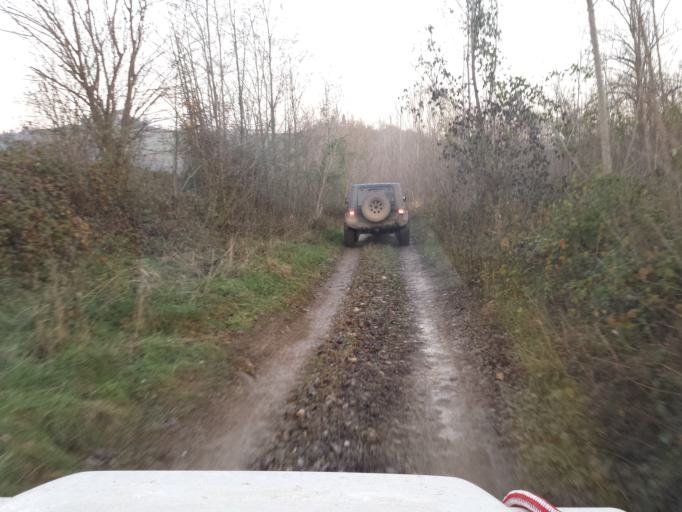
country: IT
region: Friuli Venezia Giulia
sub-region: Provincia di Udine
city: Corno di Rosazzo
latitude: 45.9994
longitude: 13.4621
